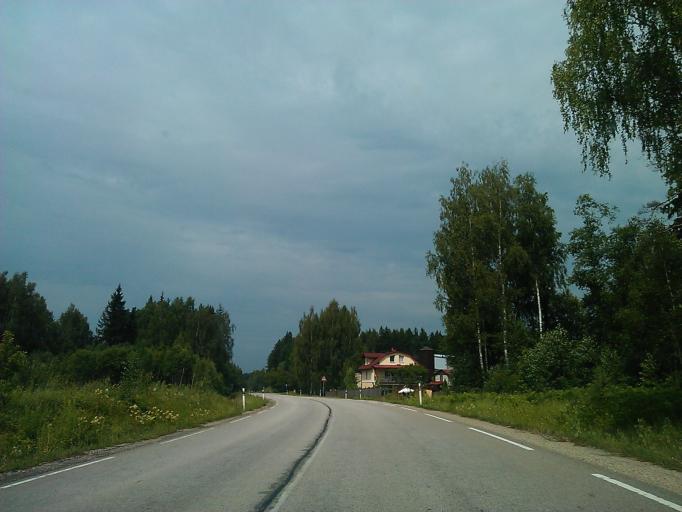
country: LV
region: Beverina
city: Murmuiza
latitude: 57.4658
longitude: 25.4141
